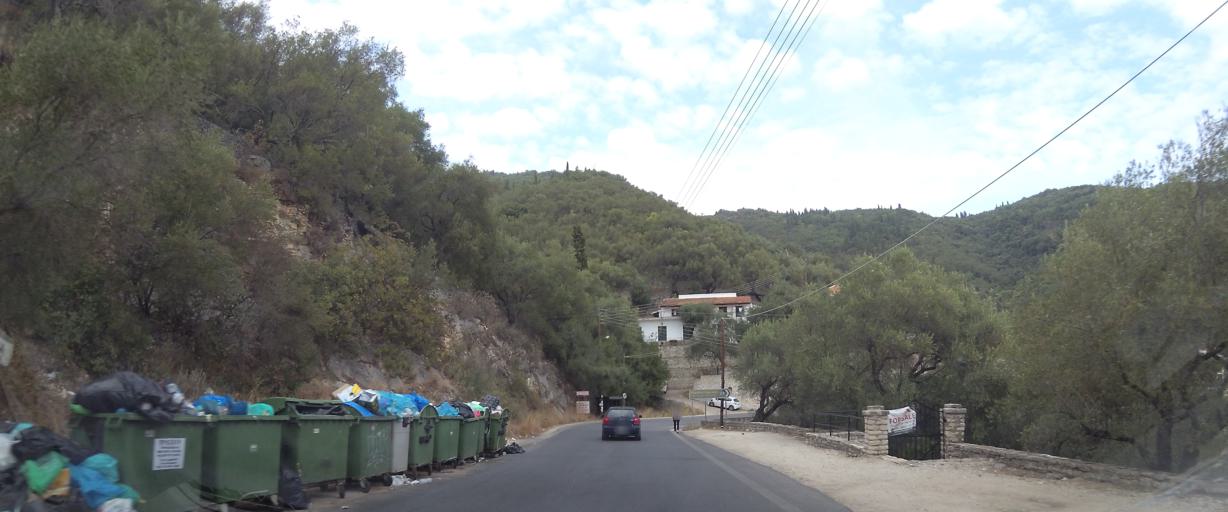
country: GR
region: Ionian Islands
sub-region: Nomos Kerkyras
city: Kontokali
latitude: 39.7301
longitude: 19.9109
